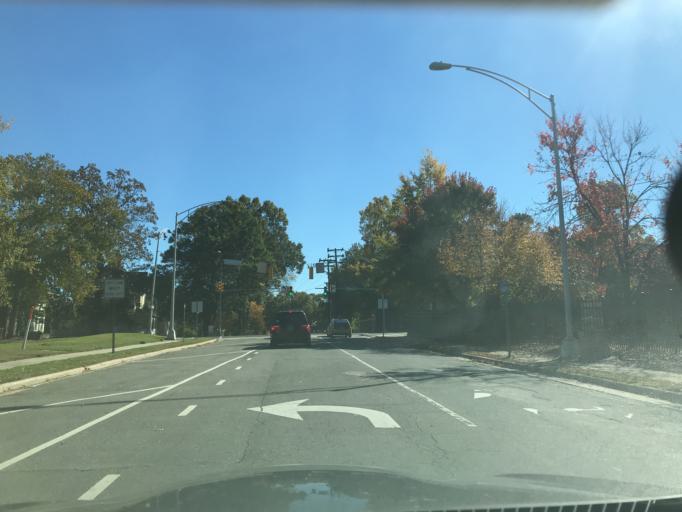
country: US
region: North Carolina
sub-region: Durham County
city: Durham
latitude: 35.9936
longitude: -78.8954
